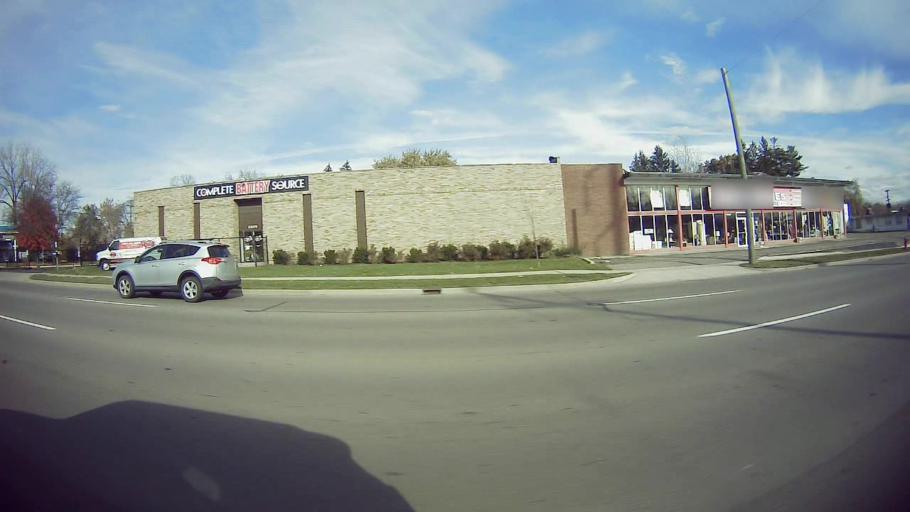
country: US
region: Michigan
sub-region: Oakland County
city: Southfield
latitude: 42.4430
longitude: -83.2715
